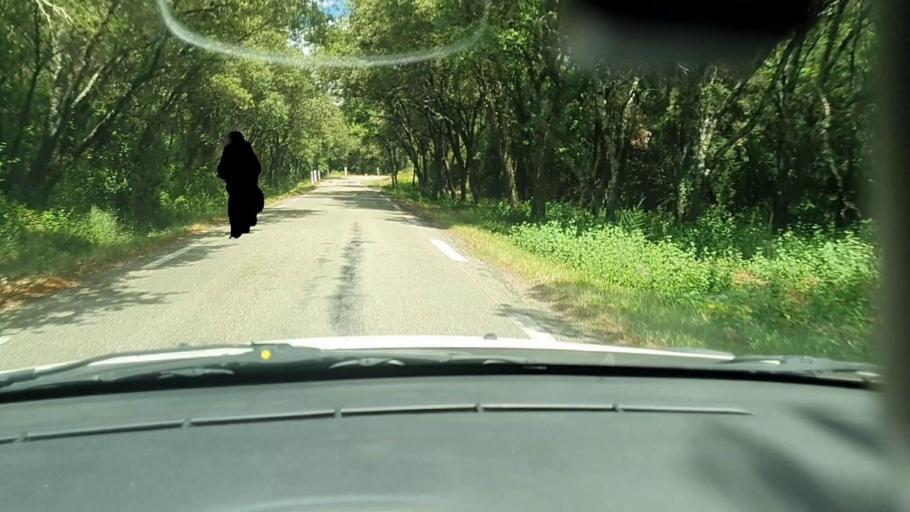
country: FR
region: Languedoc-Roussillon
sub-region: Departement du Gard
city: Cabrieres
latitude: 43.9278
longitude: 4.4719
